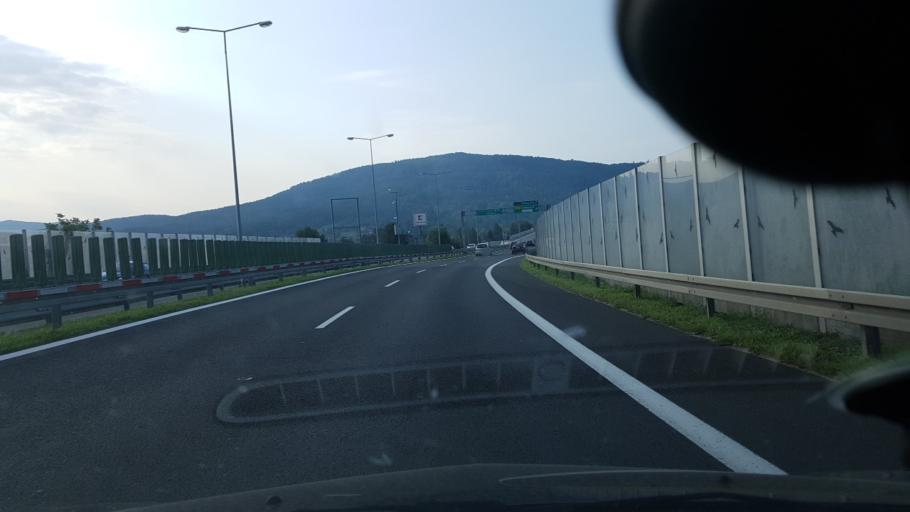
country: PL
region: Lesser Poland Voivodeship
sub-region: Powiat myslenicki
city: Myslenice
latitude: 49.8377
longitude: 19.9484
